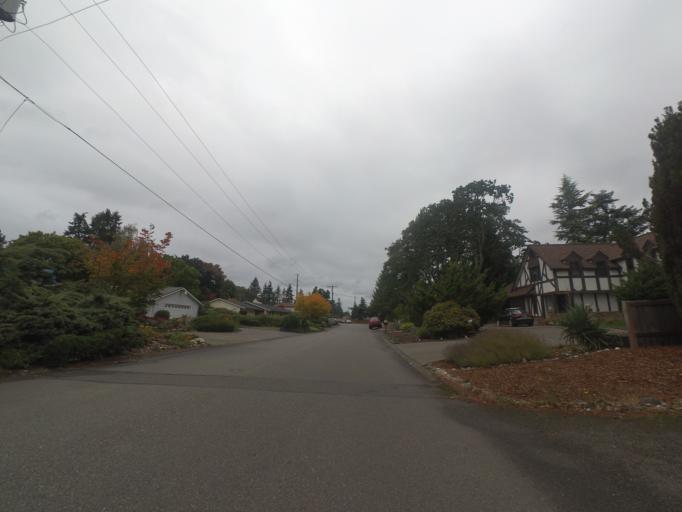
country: US
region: Washington
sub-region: Pierce County
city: Lakewood
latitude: 47.1546
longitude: -122.5132
